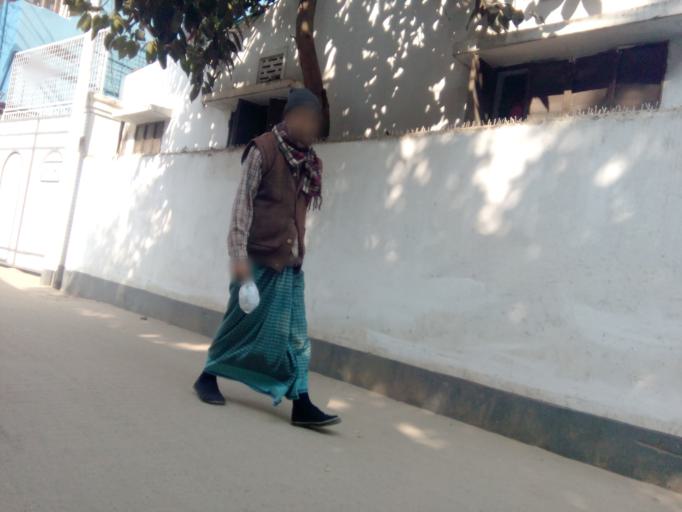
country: BD
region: Dhaka
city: Paltan
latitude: 23.7463
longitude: 90.4180
